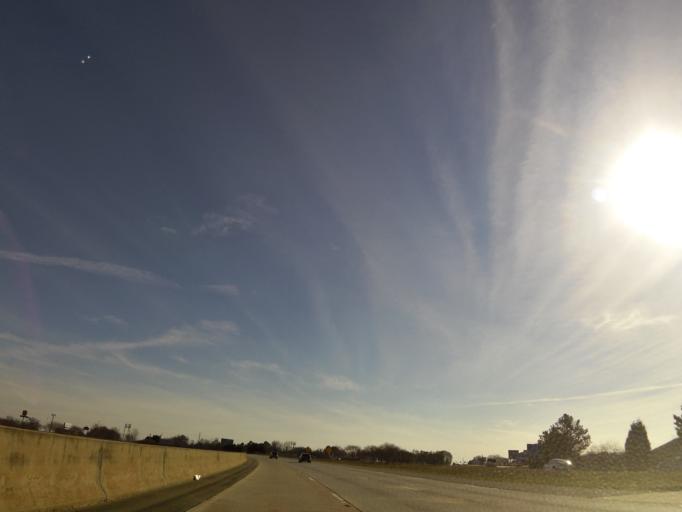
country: US
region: Georgia
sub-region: Muscogee County
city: Columbus
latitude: 32.5092
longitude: -84.9505
